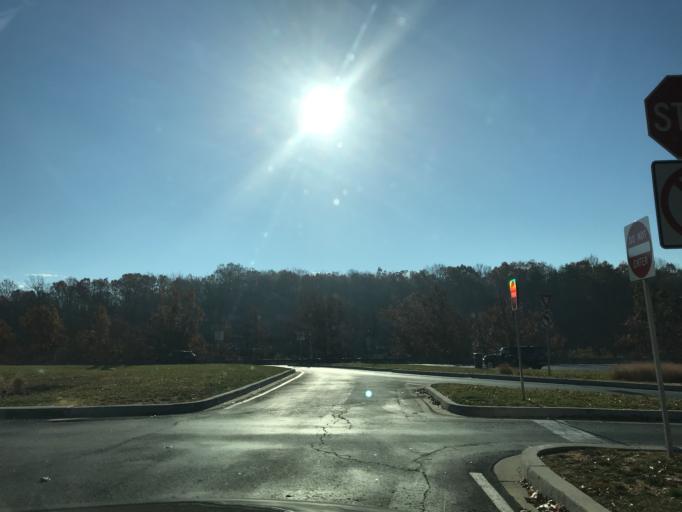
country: US
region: Maryland
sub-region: Cecil County
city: Charlestown
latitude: 39.6110
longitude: -76.0099
